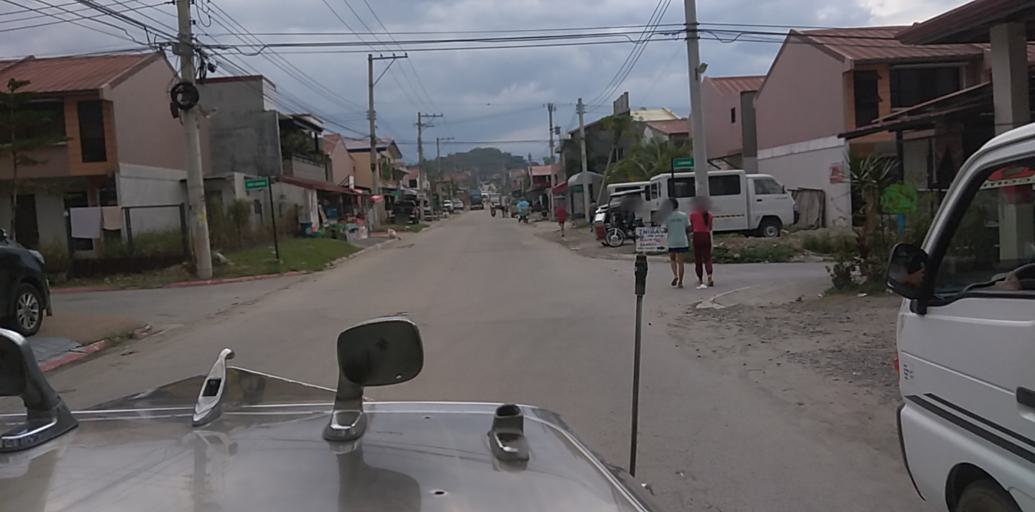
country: PH
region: Central Luzon
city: Santol
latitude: 15.1665
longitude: 120.5323
